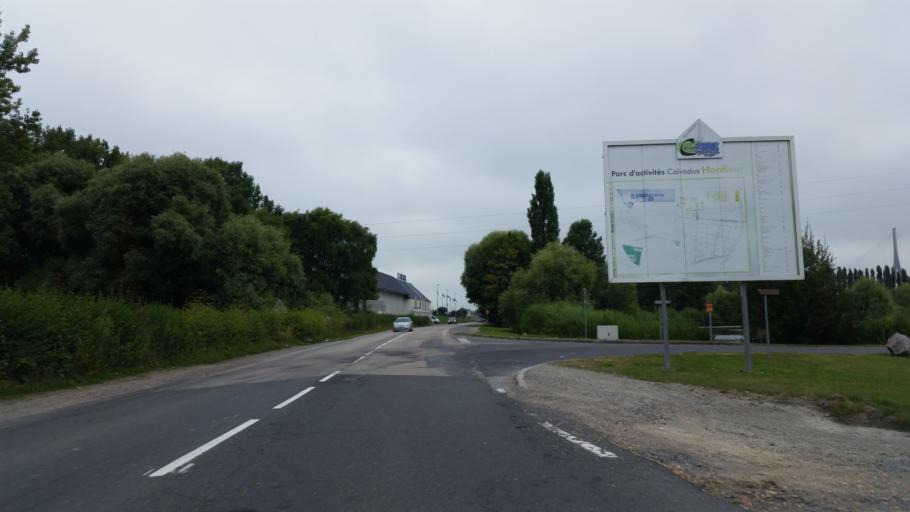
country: FR
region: Lower Normandy
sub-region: Departement du Calvados
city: La Riviere-Saint-Sauveur
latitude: 49.4123
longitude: 0.2591
